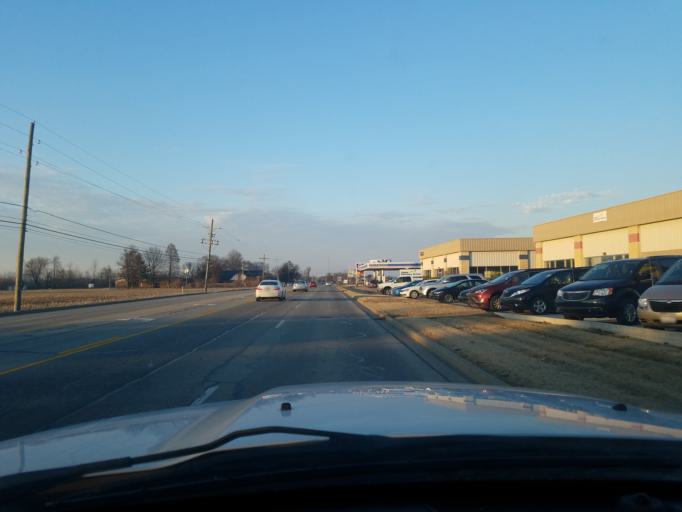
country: US
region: Indiana
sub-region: Vanderburgh County
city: Melody Hill
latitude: 38.0089
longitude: -87.4737
